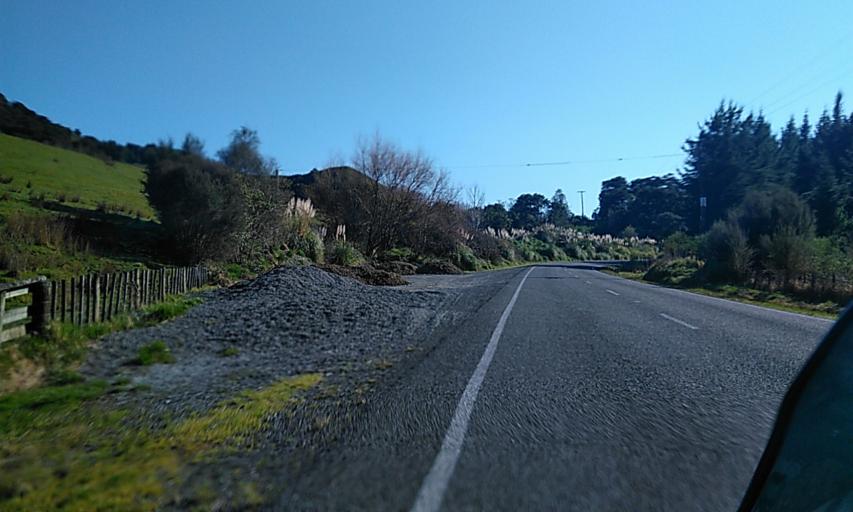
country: NZ
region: Gisborne
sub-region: Gisborne District
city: Gisborne
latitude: -38.5743
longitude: 178.0189
